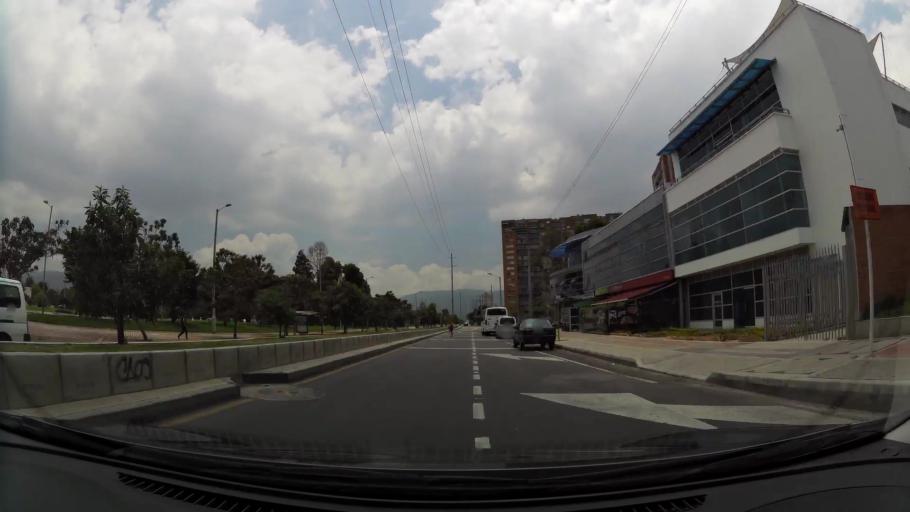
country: CO
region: Cundinamarca
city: Cota
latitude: 4.7550
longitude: -74.0636
